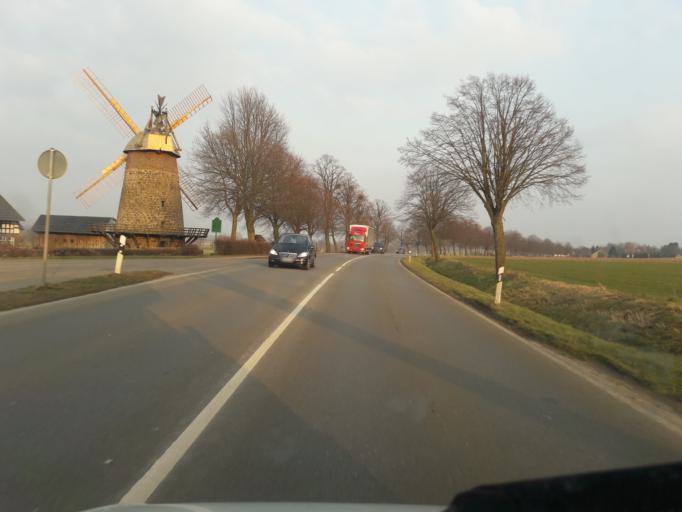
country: DE
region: North Rhine-Westphalia
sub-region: Regierungsbezirk Detmold
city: Huellhorst
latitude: 52.3097
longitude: 8.6726
